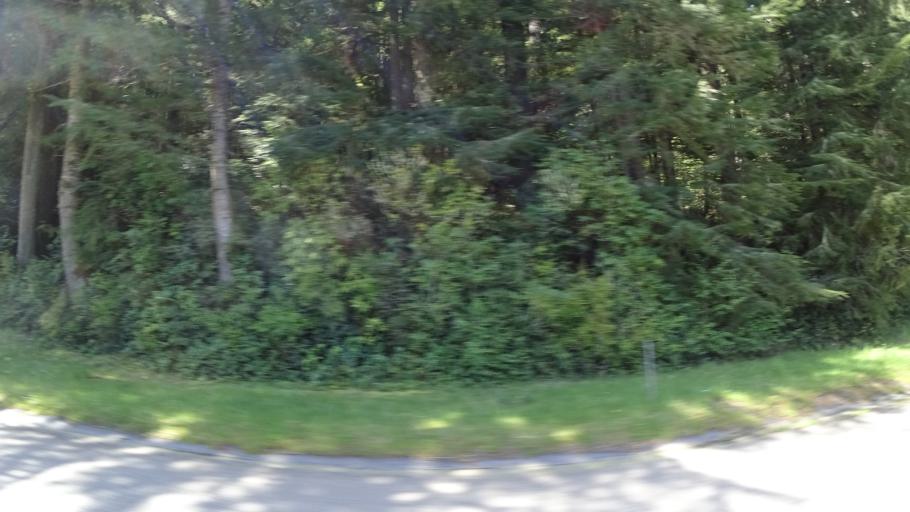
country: US
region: California
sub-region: Humboldt County
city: Westhaven-Moonstone
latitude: 41.4042
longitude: -123.9955
